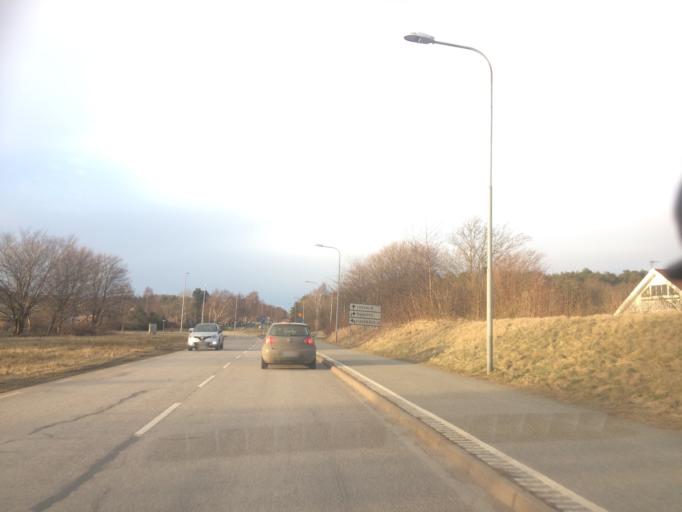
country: SE
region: Vaestra Goetaland
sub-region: Goteborg
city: Majorna
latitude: 57.6468
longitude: 11.8680
